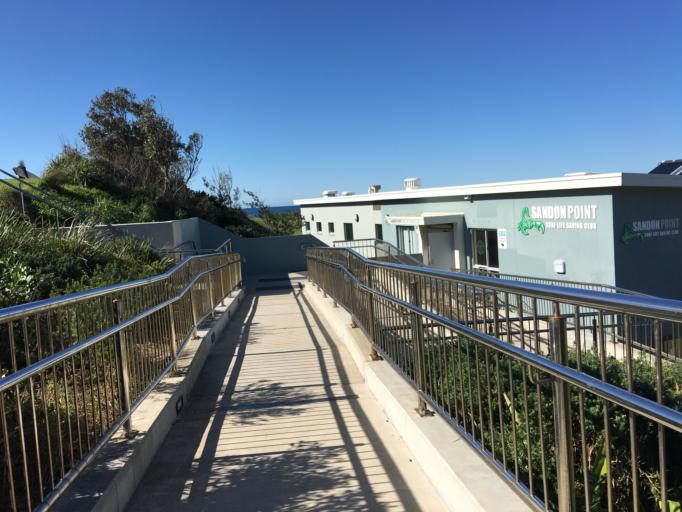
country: AU
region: New South Wales
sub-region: Wollongong
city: Bulli
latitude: -34.3308
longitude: 150.9277
